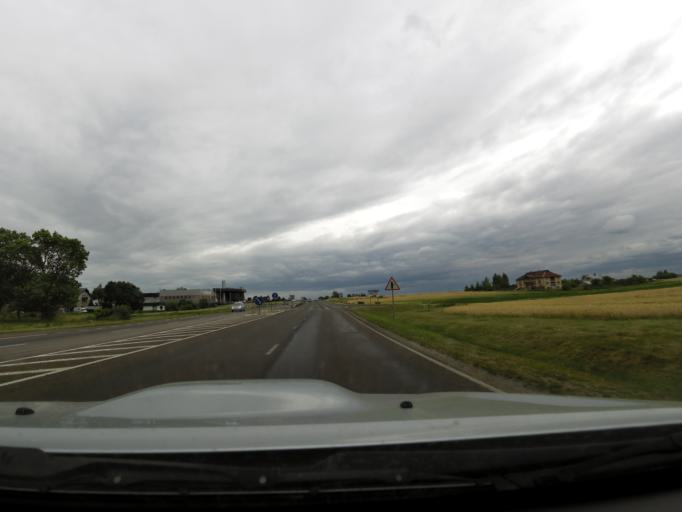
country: LT
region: Panevezys
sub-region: Panevezys City
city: Panevezys
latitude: 55.7010
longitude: 24.3814
